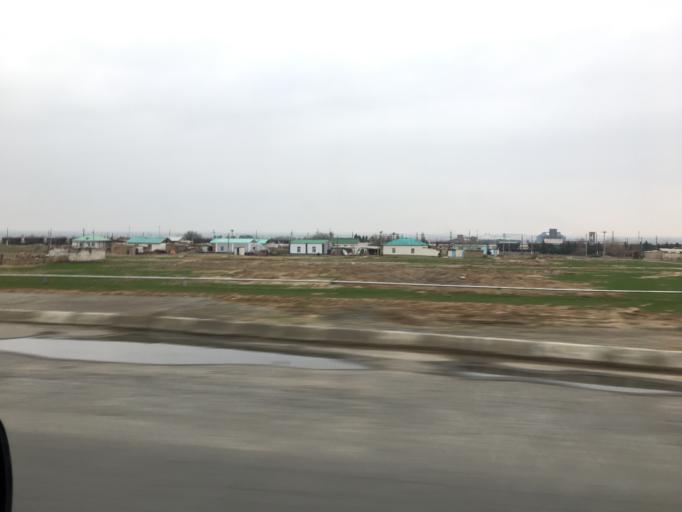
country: IR
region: Razavi Khorasan
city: Dargaz
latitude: 37.7675
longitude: 58.8978
